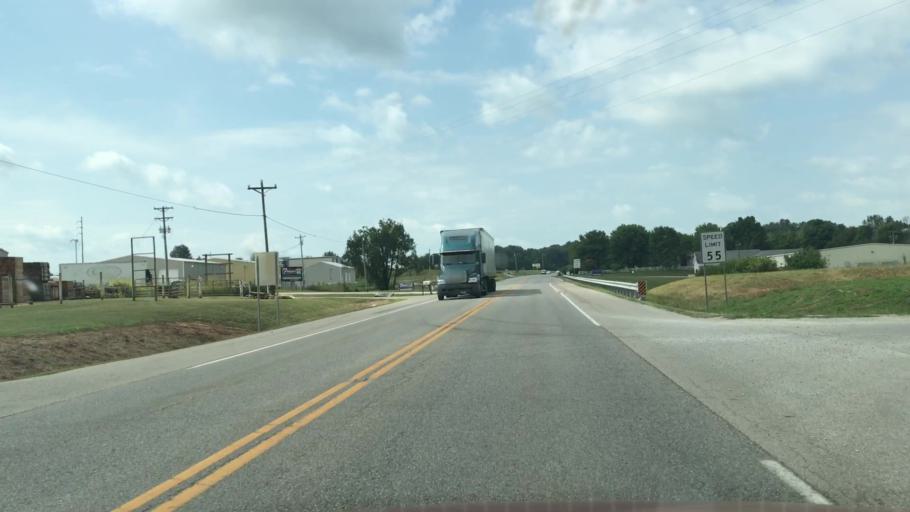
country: US
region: Kentucky
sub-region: Barren County
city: Cave City
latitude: 37.1206
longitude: -85.9623
